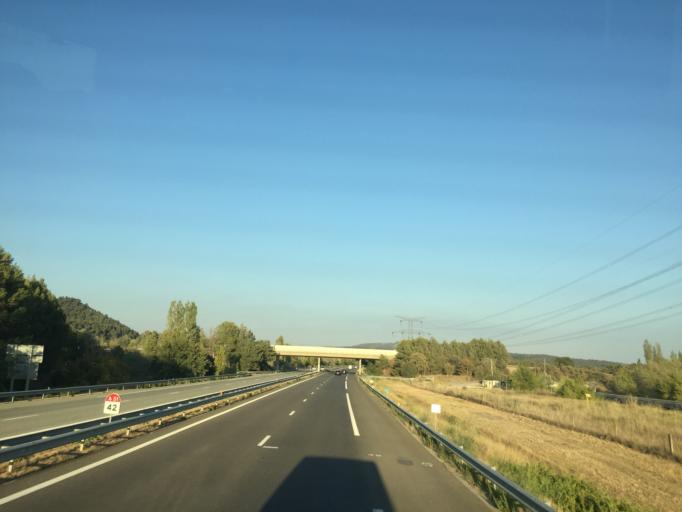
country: FR
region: Provence-Alpes-Cote d'Azur
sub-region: Departement des Bouches-du-Rhone
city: Peyrolles-en-Provence
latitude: 43.6587
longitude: 5.5773
